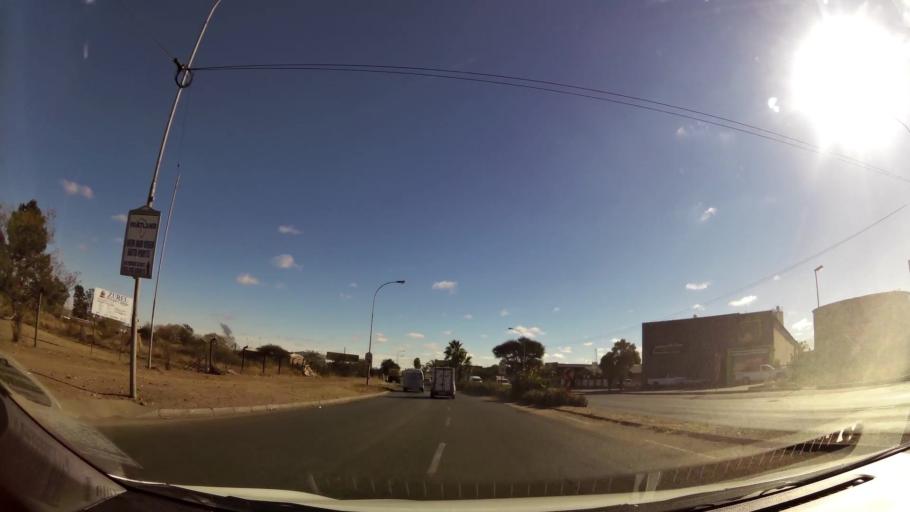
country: ZA
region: Limpopo
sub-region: Capricorn District Municipality
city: Polokwane
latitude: -23.8917
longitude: 29.4474
